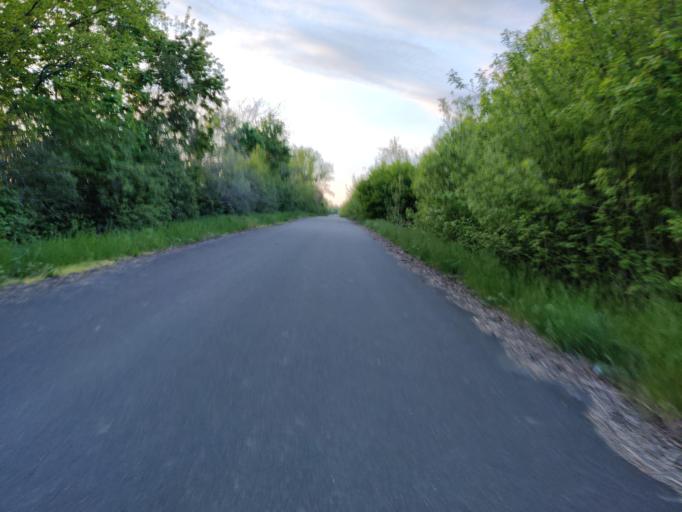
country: DE
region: Saxony
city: Bohlen
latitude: 51.2344
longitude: 12.3678
